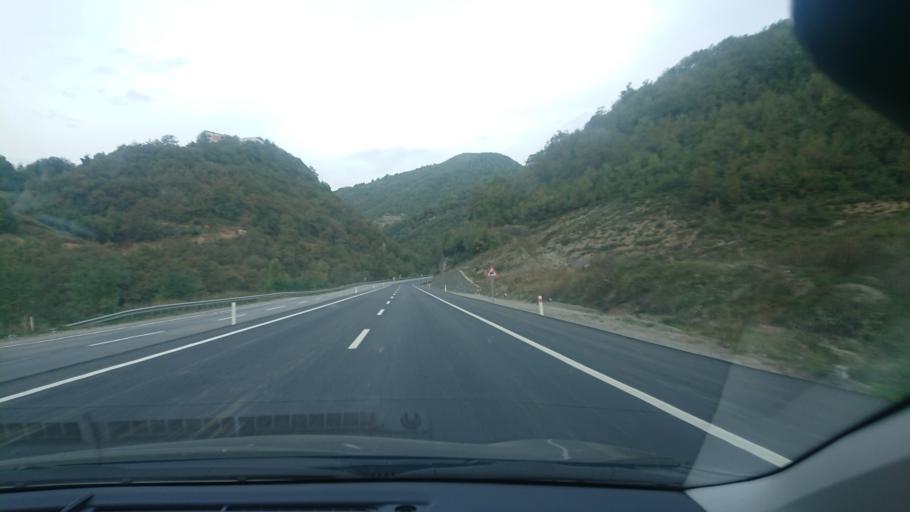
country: TR
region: Zonguldak
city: Beycuma
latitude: 41.3860
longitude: 31.9396
